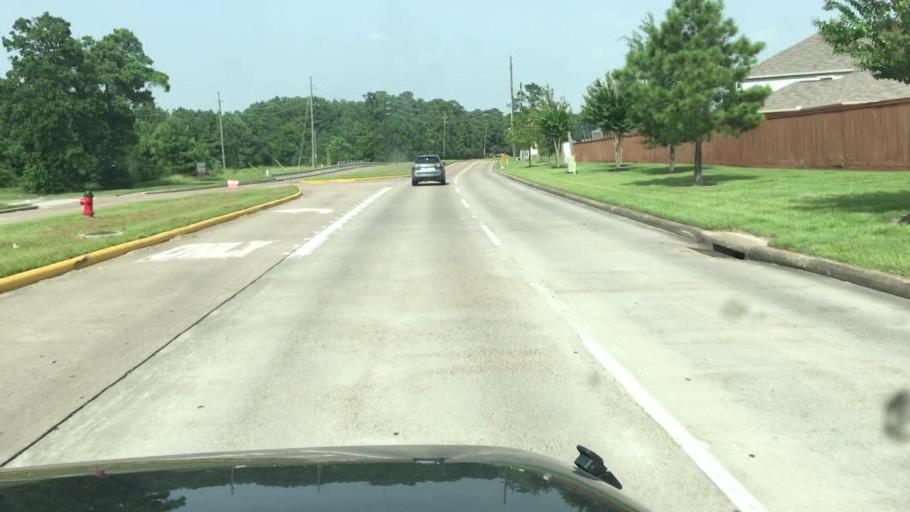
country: US
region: Texas
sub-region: Harris County
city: Atascocita
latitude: 29.9790
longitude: -95.1973
